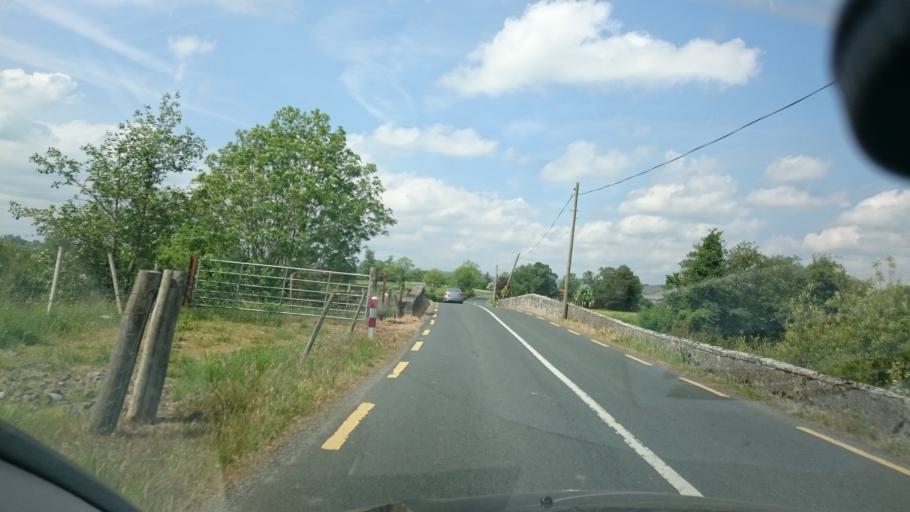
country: IE
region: Connaught
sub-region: Sligo
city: Tobercurry
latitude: 54.0575
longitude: -8.8140
